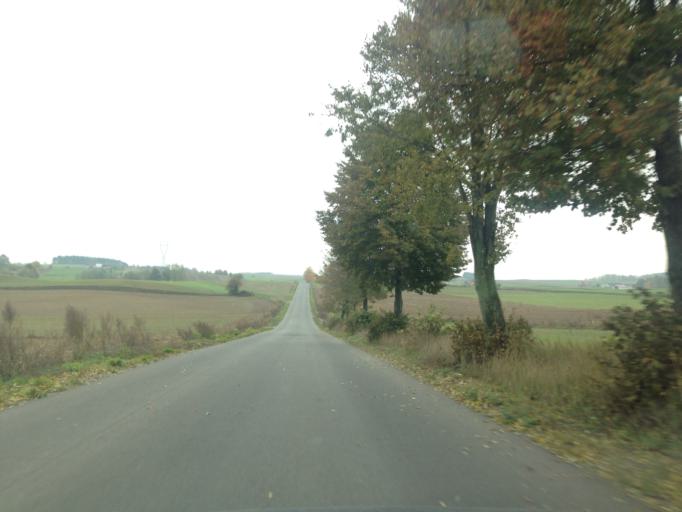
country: PL
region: Kujawsko-Pomorskie
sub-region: Powiat brodnicki
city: Brzozie
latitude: 53.3151
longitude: 19.7111
